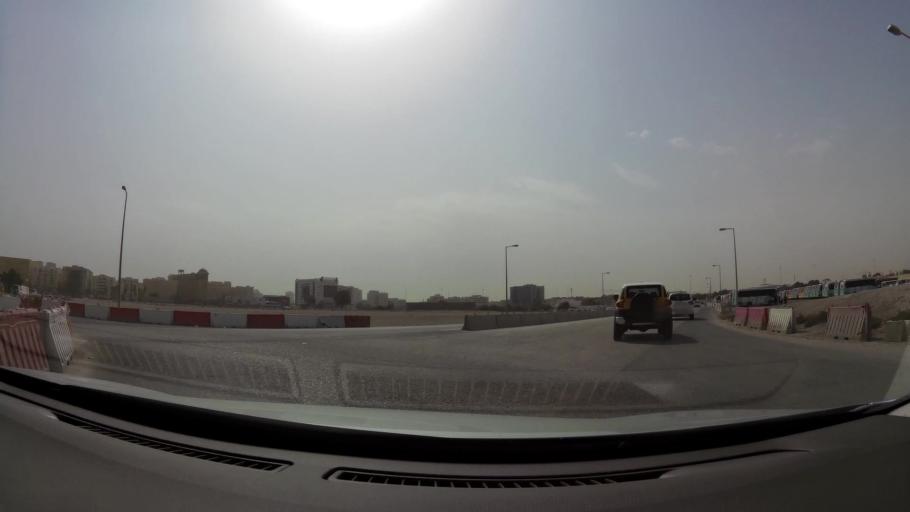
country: QA
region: Baladiyat ad Dawhah
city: Doha
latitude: 25.2849
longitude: 51.4901
